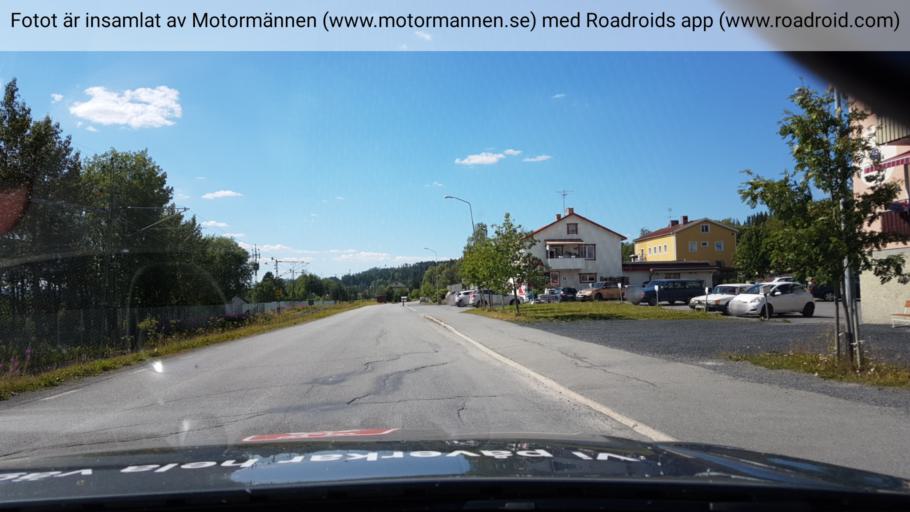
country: SE
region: Jaemtland
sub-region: Are Kommun
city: Jarpen
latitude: 63.3071
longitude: 13.6681
